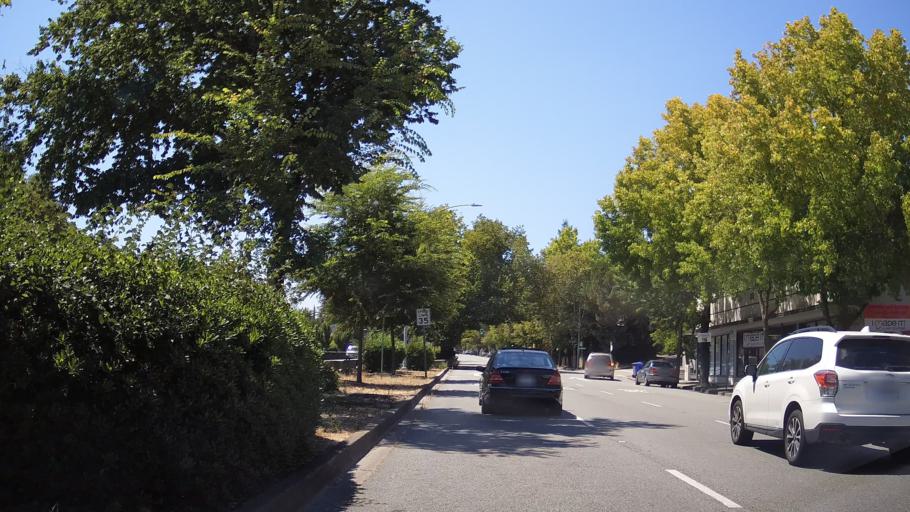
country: US
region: California
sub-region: Marin County
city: San Rafael
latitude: 37.9745
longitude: -122.5423
